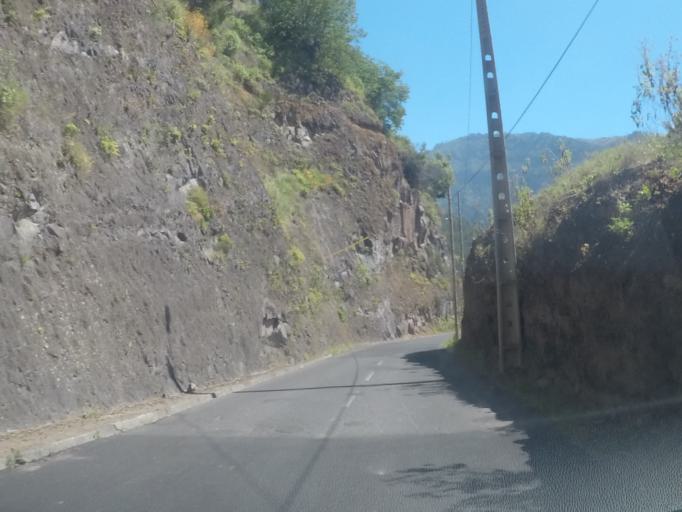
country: PT
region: Madeira
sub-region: Camara de Lobos
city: Curral das Freiras
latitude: 32.6898
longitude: -16.9711
